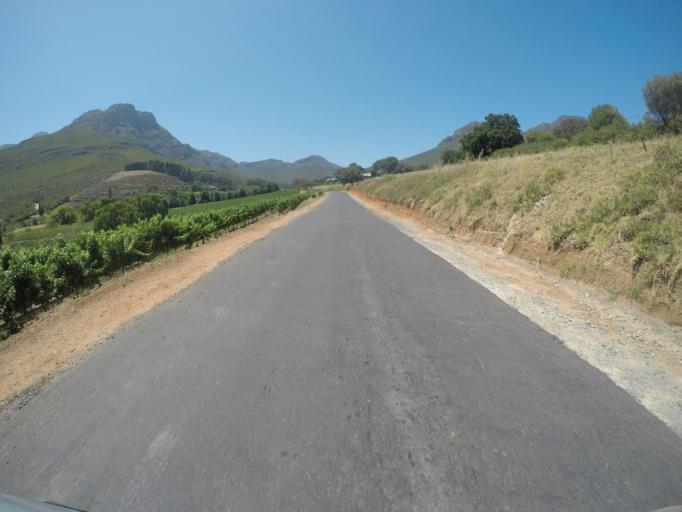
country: ZA
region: Western Cape
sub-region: Cape Winelands District Municipality
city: Stellenbosch
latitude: -33.9993
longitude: 18.8829
